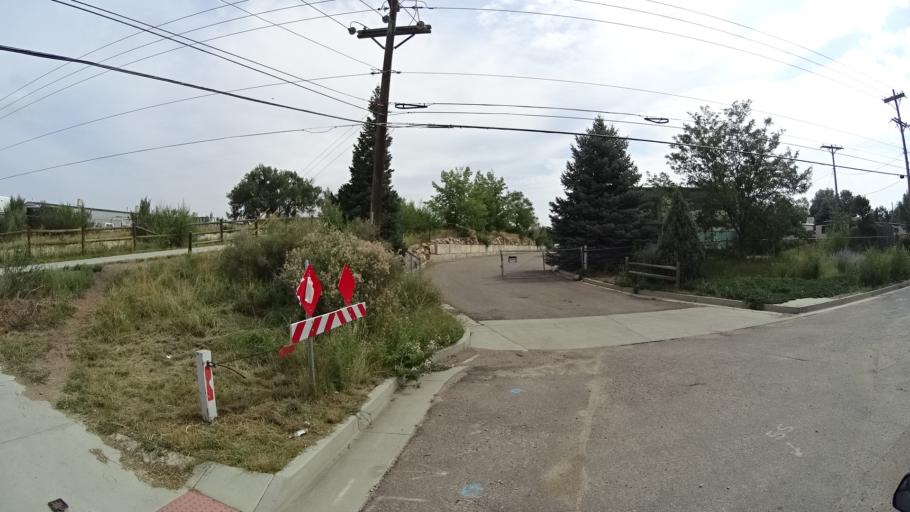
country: US
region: Colorado
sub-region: El Paso County
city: Colorado Springs
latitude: 38.8886
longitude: -104.8231
